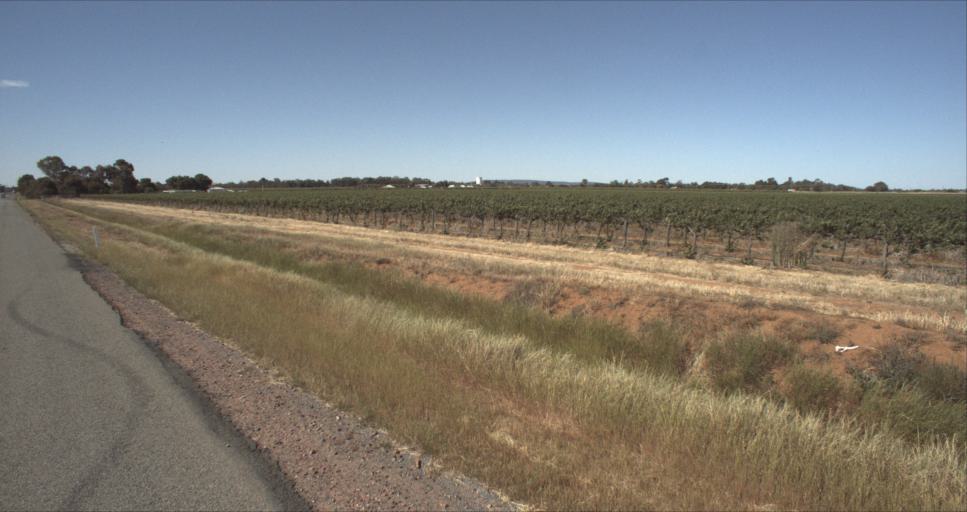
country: AU
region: New South Wales
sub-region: Leeton
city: Leeton
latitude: -34.5717
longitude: 146.3815
